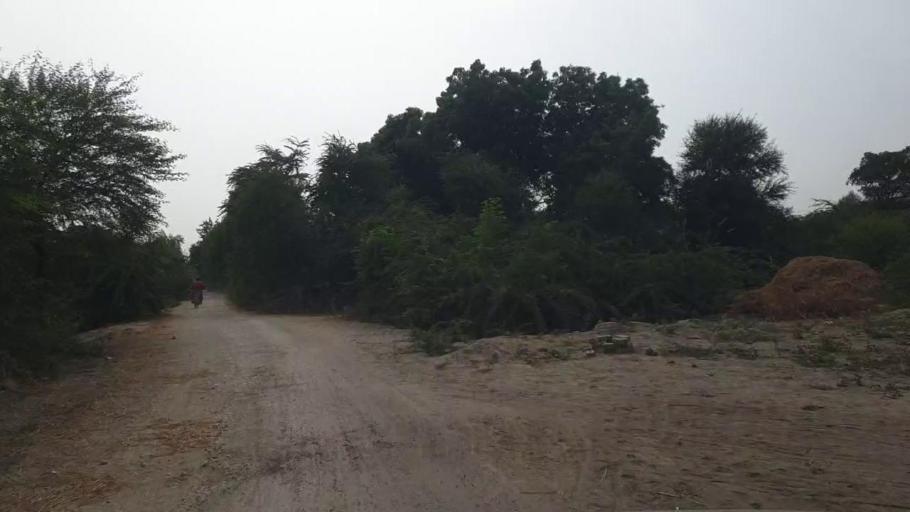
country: PK
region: Sindh
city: Matli
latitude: 24.9896
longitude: 68.7025
